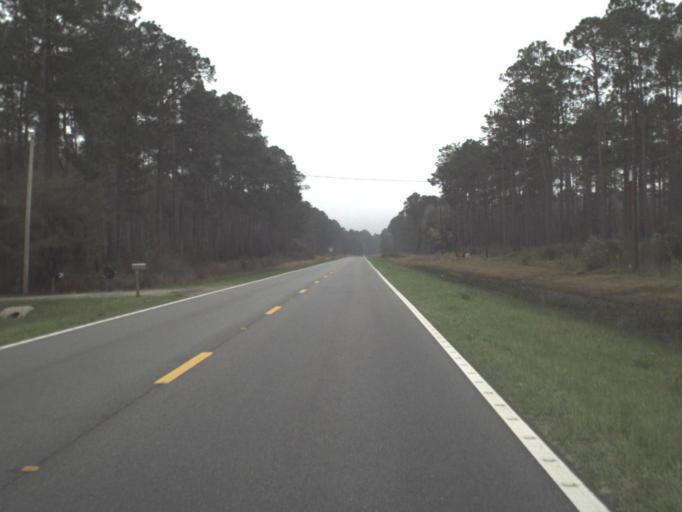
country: US
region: Florida
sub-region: Liberty County
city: Bristol
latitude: 30.3292
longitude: -84.8238
